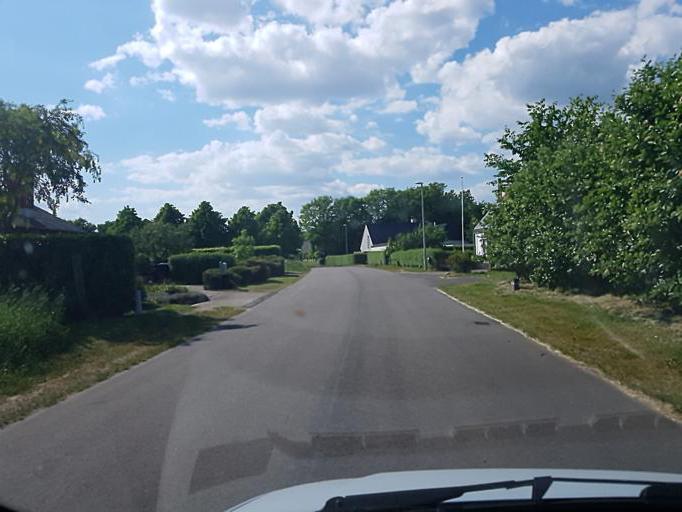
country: DK
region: South Denmark
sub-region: Esbjerg Kommune
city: Bramming
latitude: 55.4255
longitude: 8.6436
